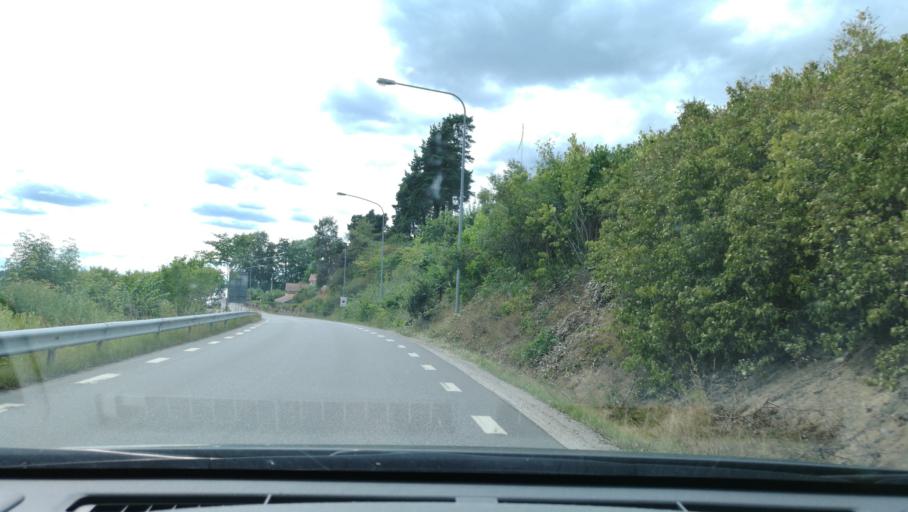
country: SE
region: OEstergoetland
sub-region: Norrkopings Kommun
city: Krokek
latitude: 58.6598
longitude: 16.3962
